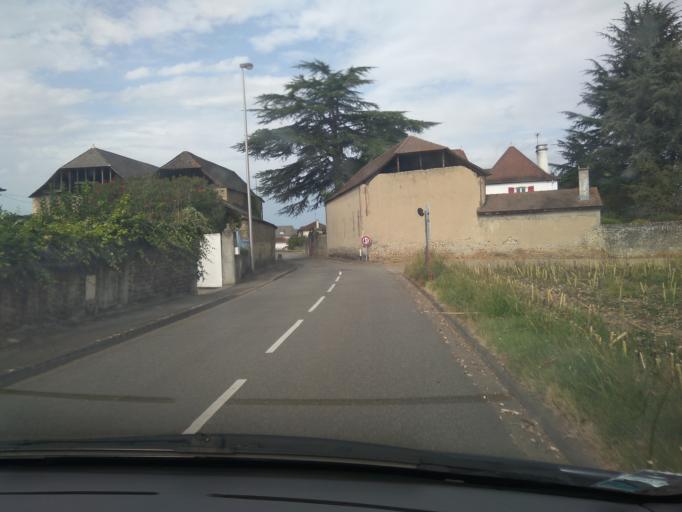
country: FR
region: Aquitaine
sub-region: Departement des Pyrenees-Atlantiques
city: Mourenx
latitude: 43.3648
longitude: -0.5795
